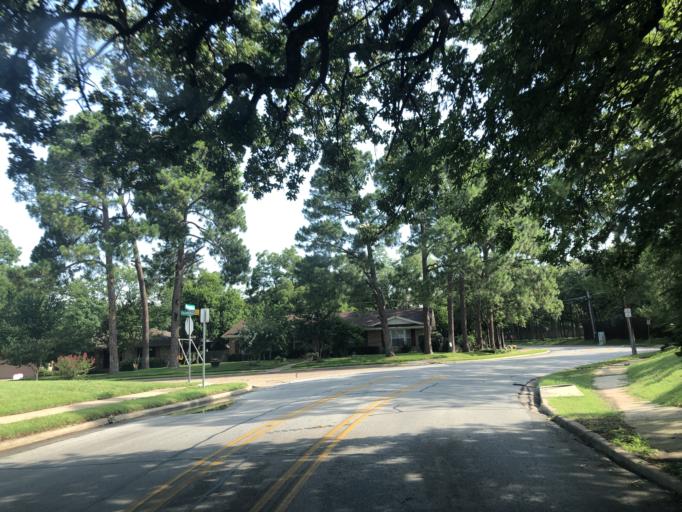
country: US
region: Texas
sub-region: Dallas County
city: Irving
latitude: 32.8005
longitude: -96.9689
